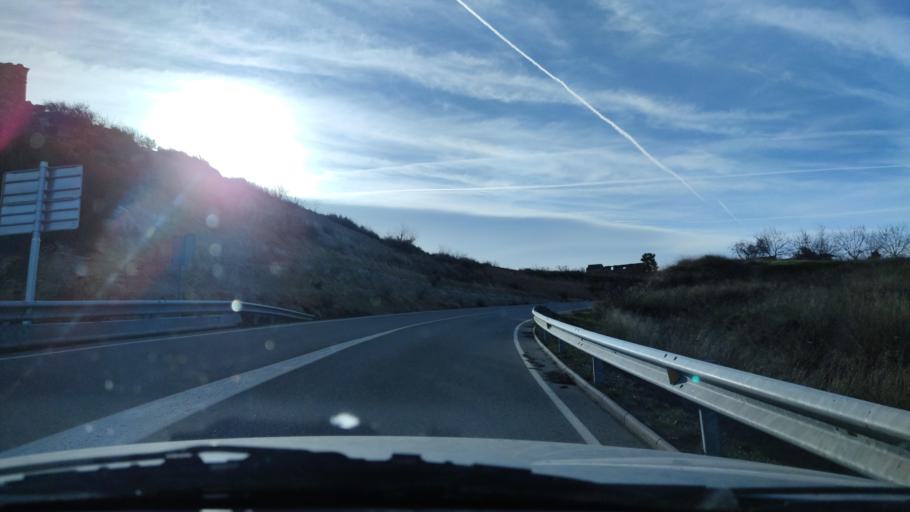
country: ES
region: Catalonia
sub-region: Provincia de Lleida
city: Aspa
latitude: 41.4946
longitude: 0.6768
